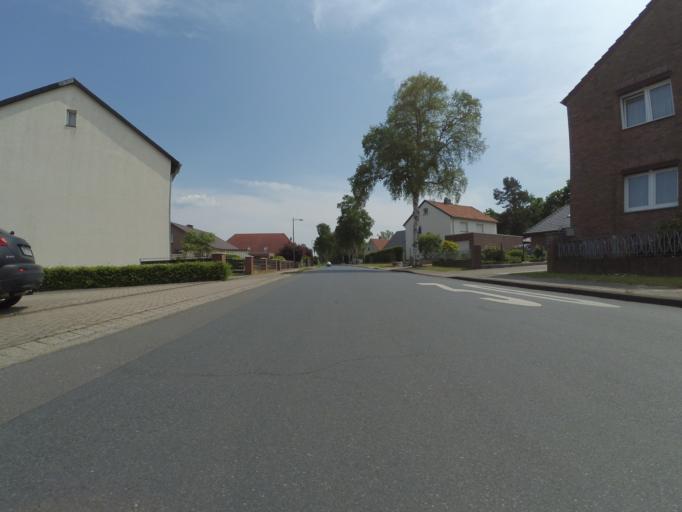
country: DE
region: Lower Saxony
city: Peine
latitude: 52.3492
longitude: 10.1874
